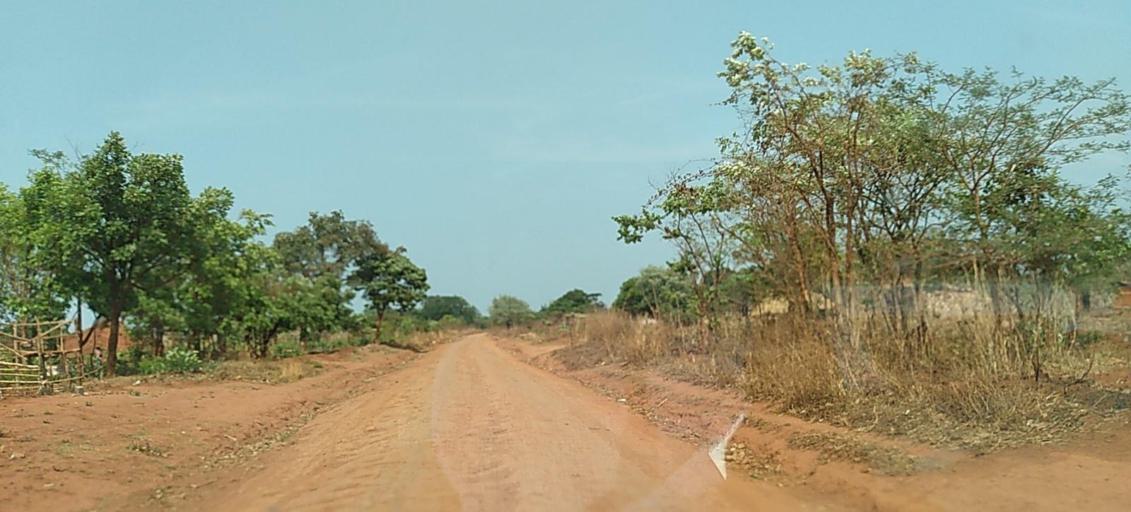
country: ZM
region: Copperbelt
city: Chililabombwe
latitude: -12.3418
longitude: 27.7096
